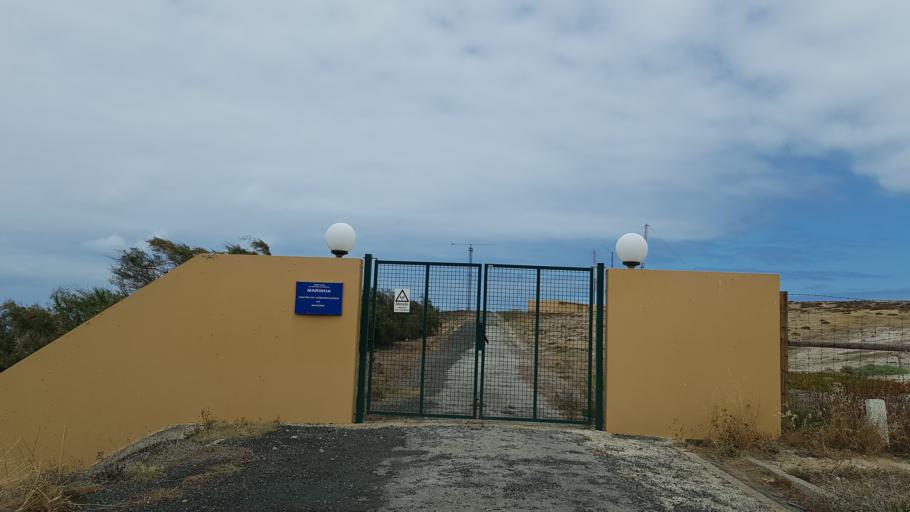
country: PT
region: Madeira
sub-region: Porto Santo
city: Camacha
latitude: 33.0927
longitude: -16.3359
